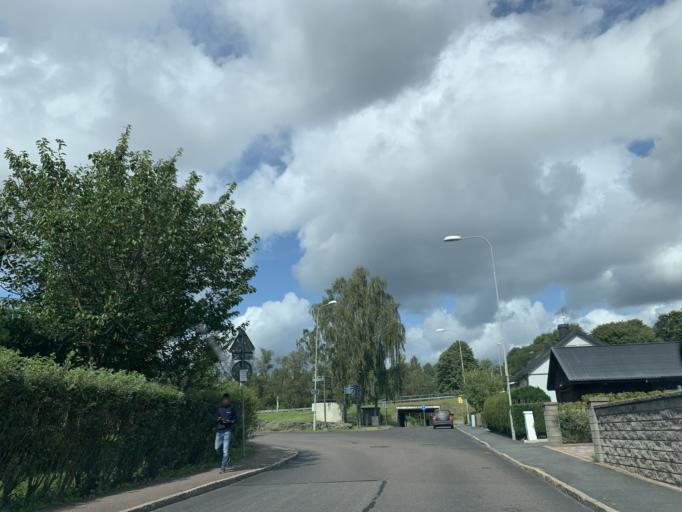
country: SE
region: Vaestra Goetaland
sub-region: Goteborg
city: Eriksbo
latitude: 57.7547
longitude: 12.0494
